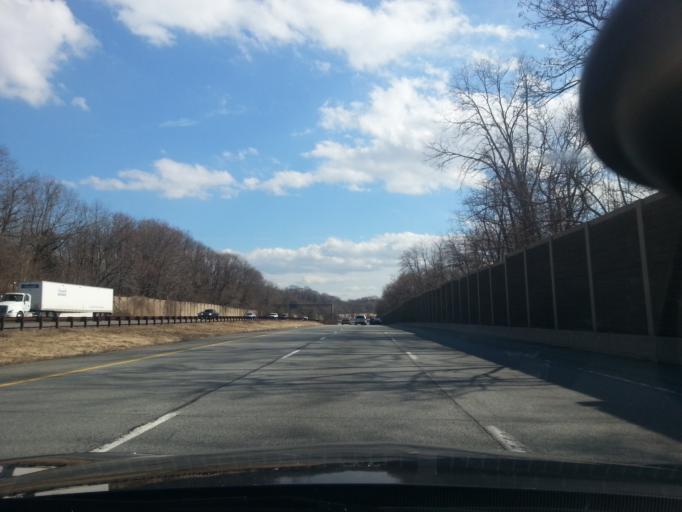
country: US
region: Pennsylvania
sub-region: Delaware County
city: Radnor
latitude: 40.0227
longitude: -75.3615
